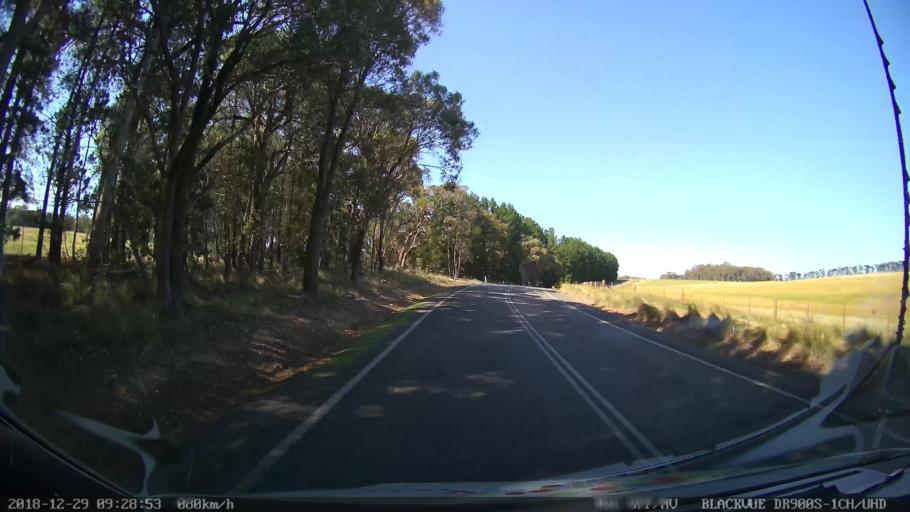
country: AU
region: New South Wales
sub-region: Upper Lachlan Shire
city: Crookwell
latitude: -34.5839
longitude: 149.3793
